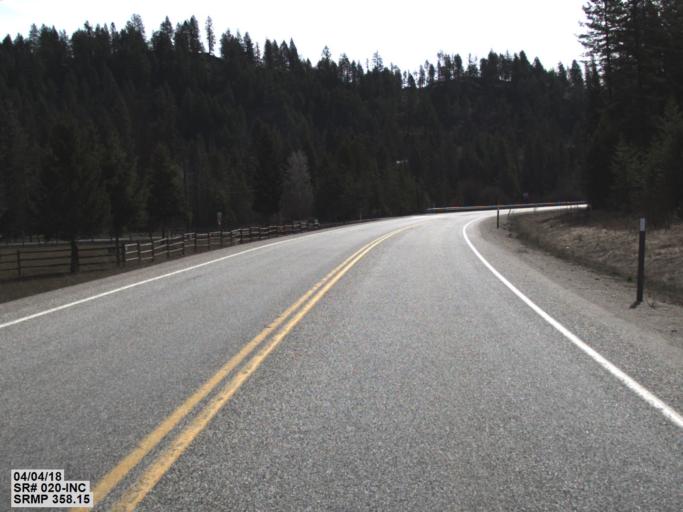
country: US
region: Washington
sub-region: Stevens County
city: Colville
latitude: 48.5396
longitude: -117.8270
